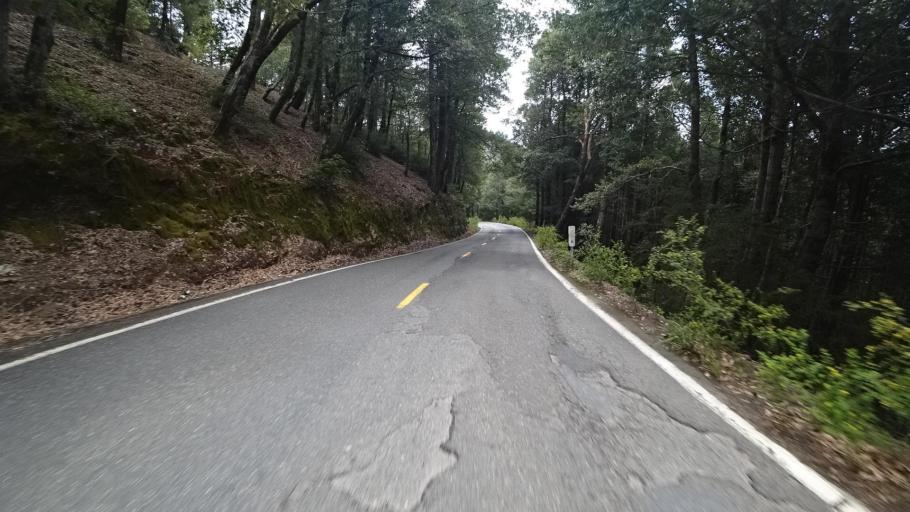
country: US
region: California
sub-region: Humboldt County
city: Redway
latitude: 40.0402
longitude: -124.0236
